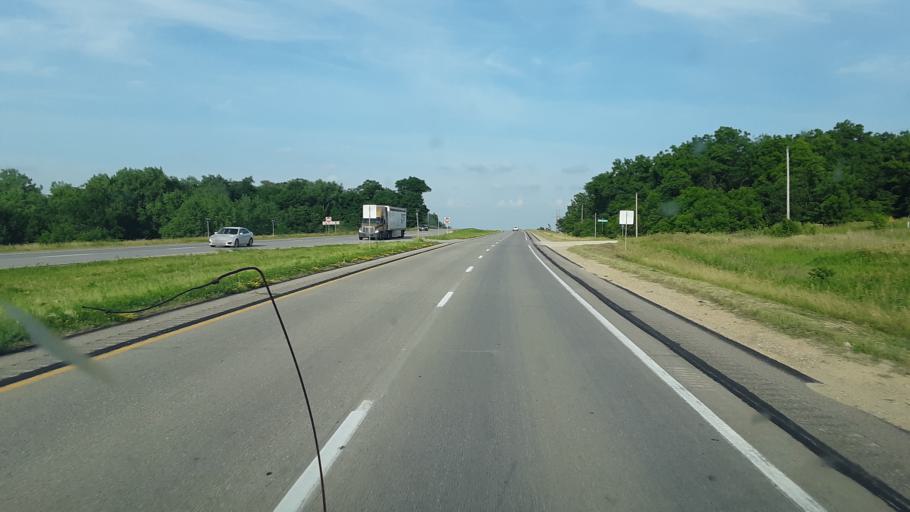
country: US
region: Iowa
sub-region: Marshall County
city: Marshalltown
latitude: 42.0069
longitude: -92.8490
